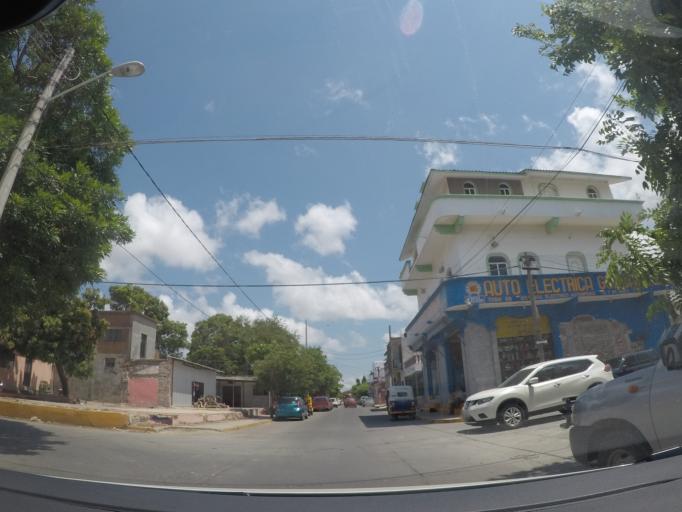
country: MX
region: Oaxaca
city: Juchitan de Zaragoza
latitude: 16.4408
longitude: -95.0221
